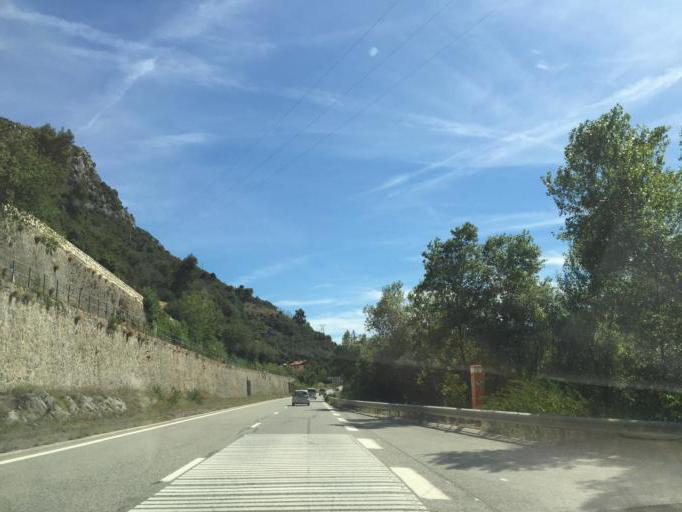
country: FR
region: Provence-Alpes-Cote d'Azur
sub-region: Departement des Alpes-Maritimes
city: Levens
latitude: 43.8639
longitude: 7.1988
